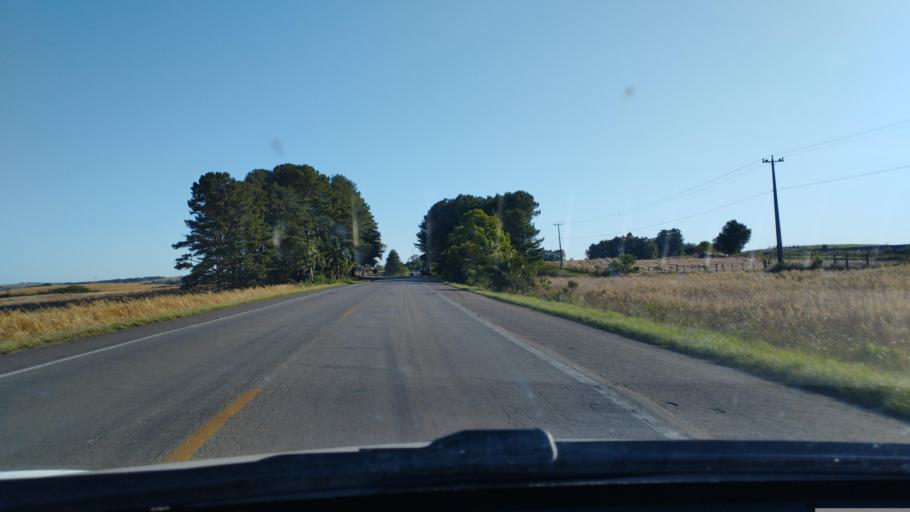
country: BR
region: Rio Grande do Sul
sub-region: Julio De Castilhos
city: Julio de Castilhos
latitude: -29.4337
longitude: -53.6762
